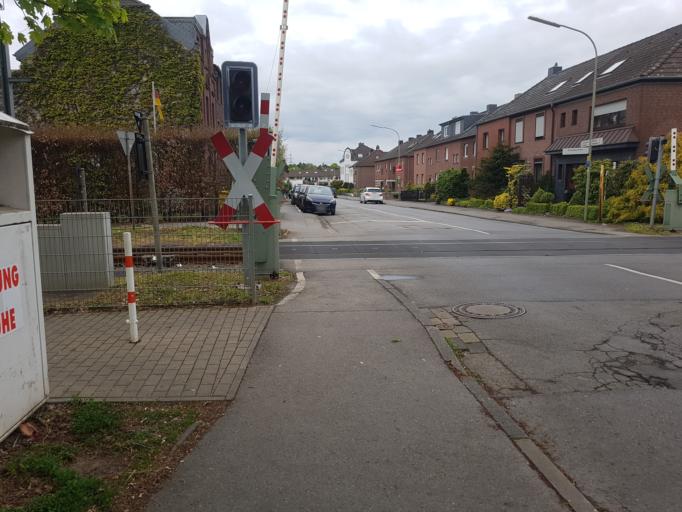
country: DE
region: North Rhine-Westphalia
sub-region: Regierungsbezirk Koln
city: Eschweiler
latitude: 50.8175
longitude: 6.2521
